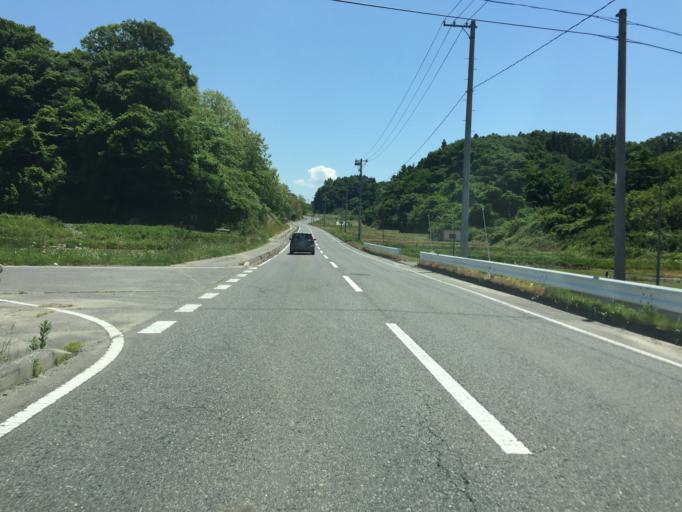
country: JP
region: Fukushima
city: Motomiya
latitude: 37.5235
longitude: 140.4499
